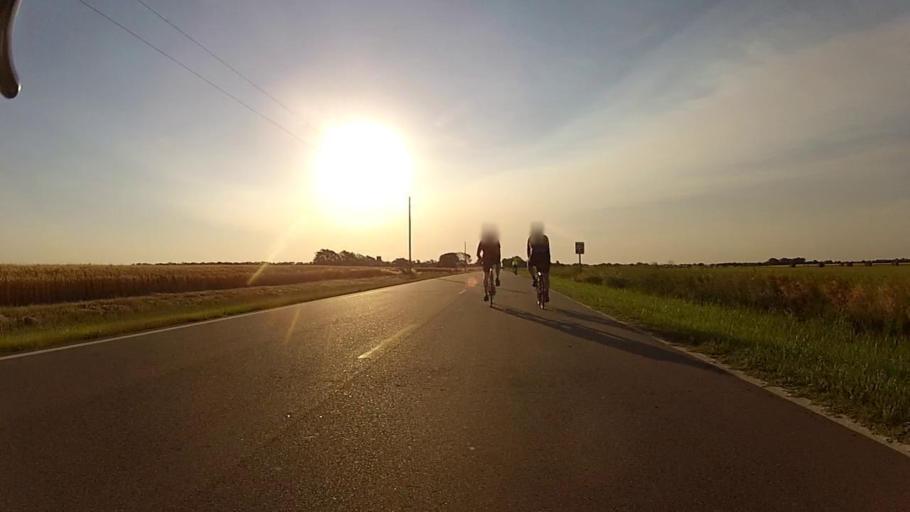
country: US
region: Kansas
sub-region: Harper County
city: Anthony
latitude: 37.1539
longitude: -97.8562
